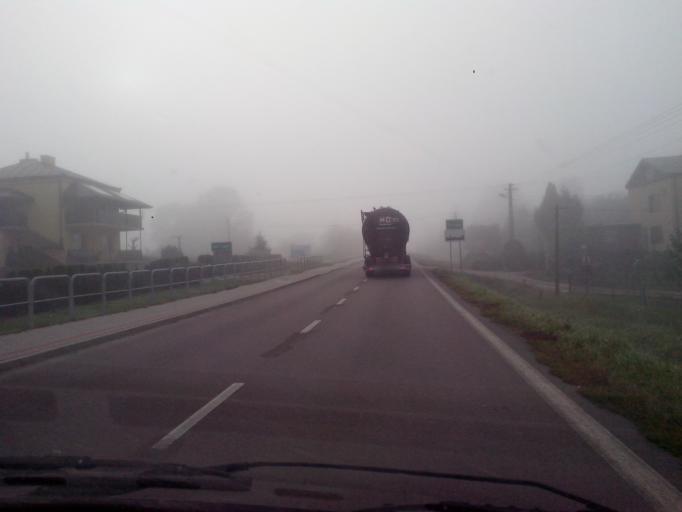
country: PL
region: Subcarpathian Voivodeship
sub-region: Przemysl
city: Przemysl
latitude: 49.7977
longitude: 22.7158
